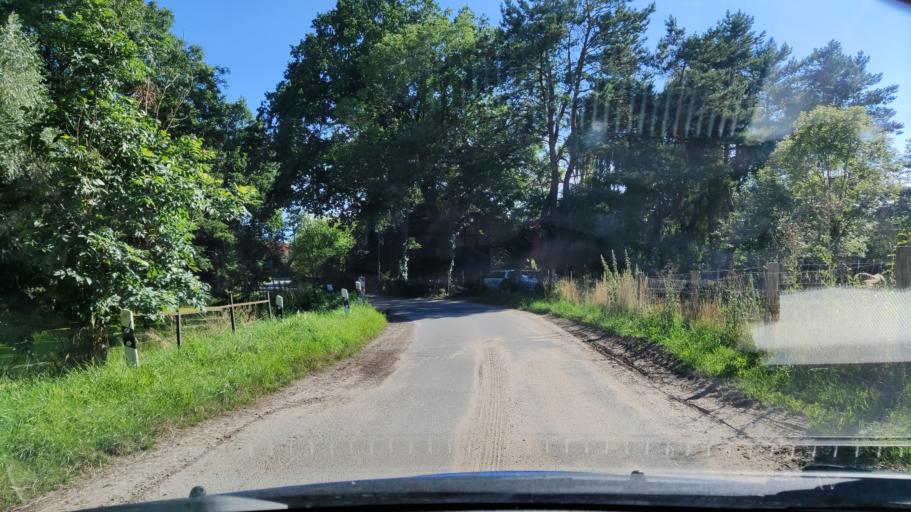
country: DE
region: Lower Saxony
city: Boitze
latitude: 53.1502
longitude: 10.7485
